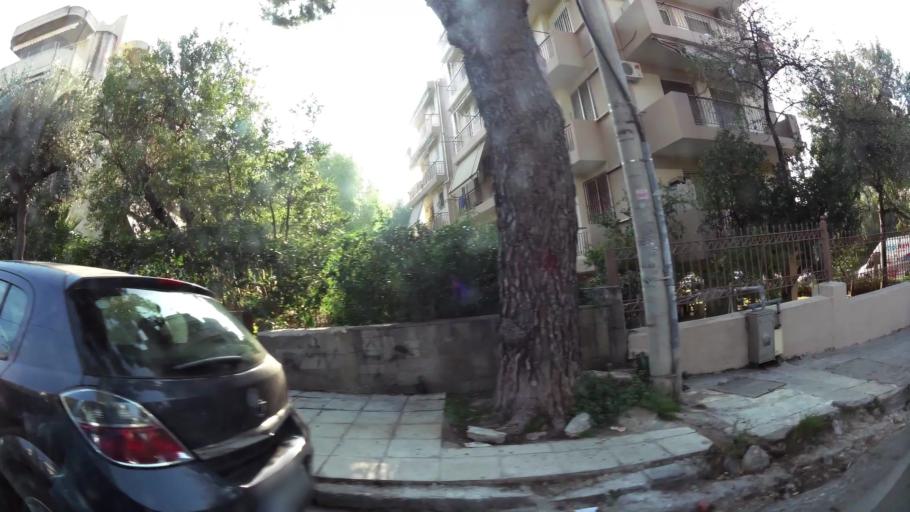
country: GR
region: Attica
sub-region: Nomarchia Athinas
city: Agia Paraskevi
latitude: 38.0071
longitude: 23.8228
